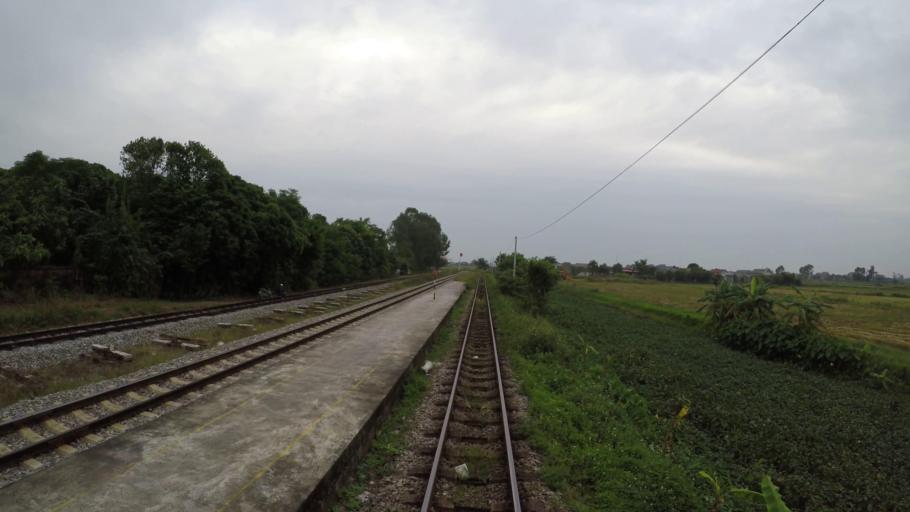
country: VN
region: Hai Duong
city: Ke Sat
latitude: 20.9663
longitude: 106.1608
